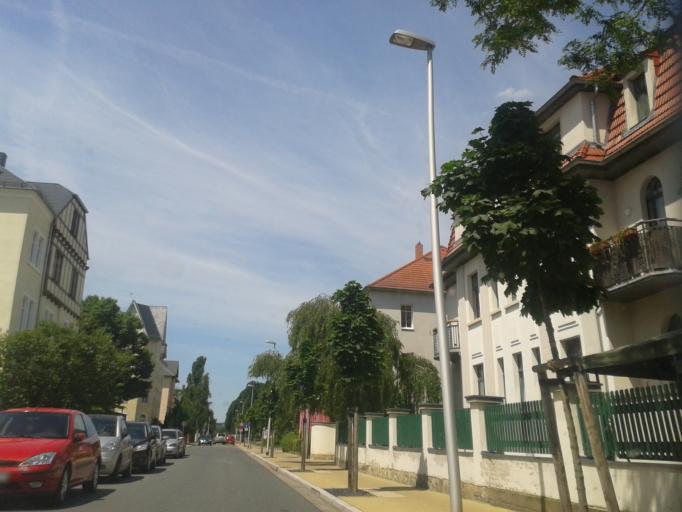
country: DE
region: Saxony
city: Radebeul
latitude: 51.0948
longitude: 13.6860
